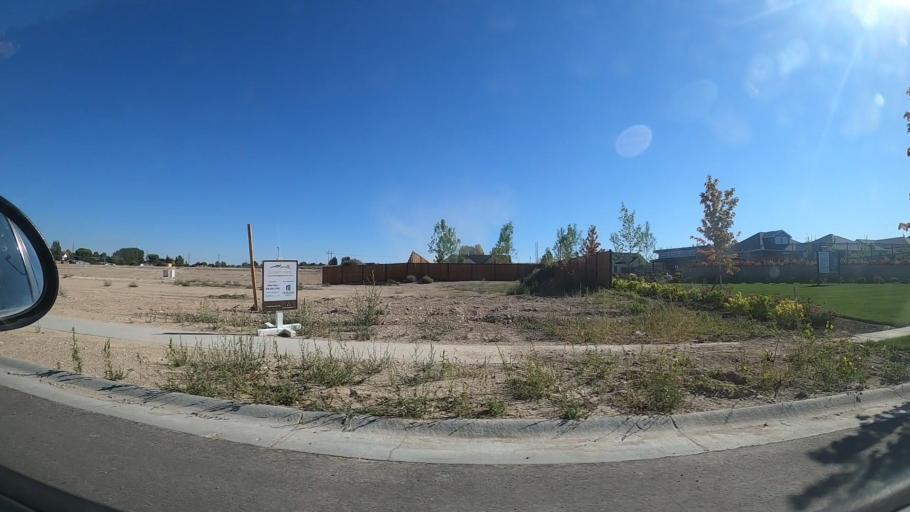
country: US
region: Idaho
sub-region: Canyon County
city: Nampa
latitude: 43.5471
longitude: -116.5974
